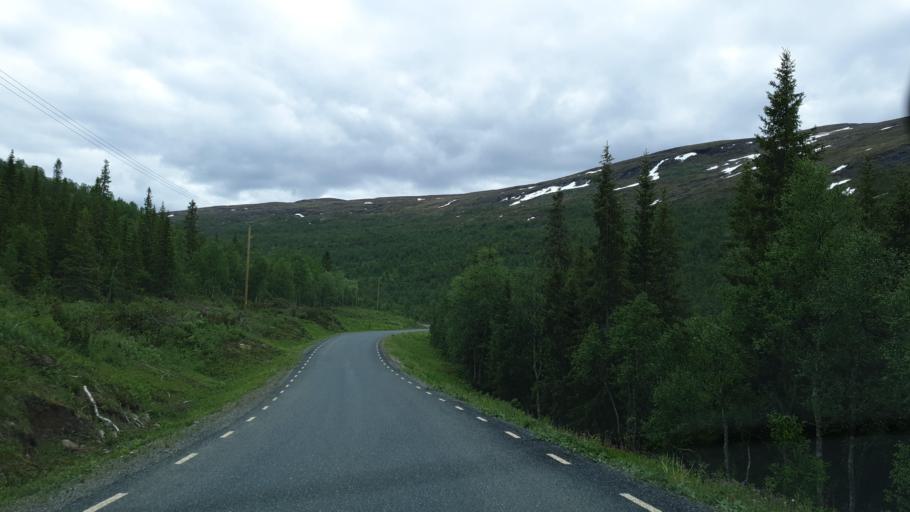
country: NO
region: Nordland
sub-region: Hattfjelldal
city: Hattfjelldal
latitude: 65.4263
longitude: 14.6016
